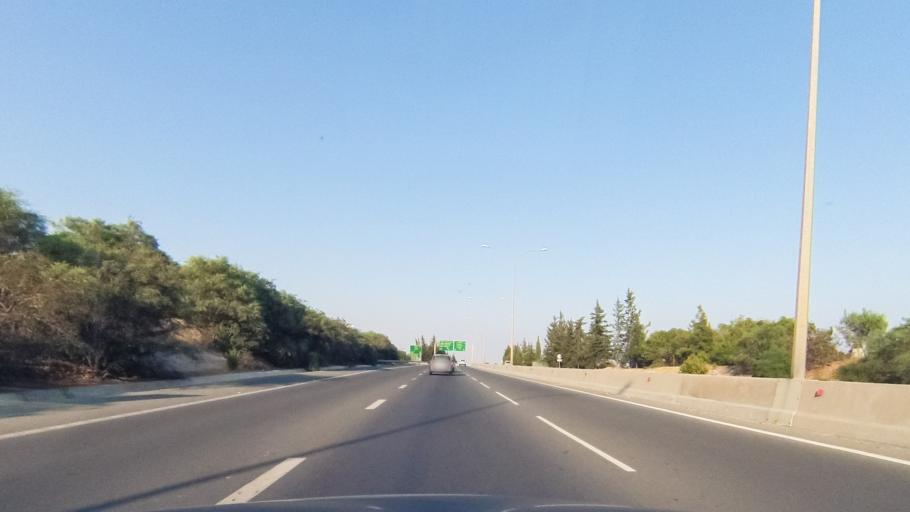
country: CY
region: Limassol
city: Limassol
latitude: 34.7053
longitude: 33.0358
